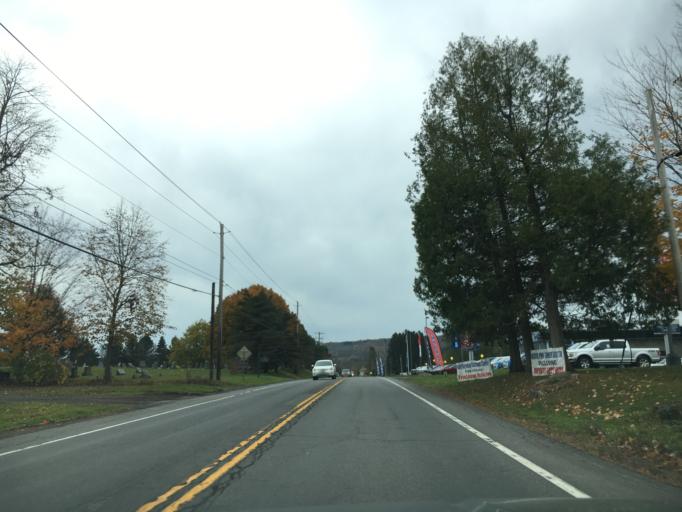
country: US
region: New York
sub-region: Otsego County
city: Cooperstown
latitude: 42.6714
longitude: -74.9527
